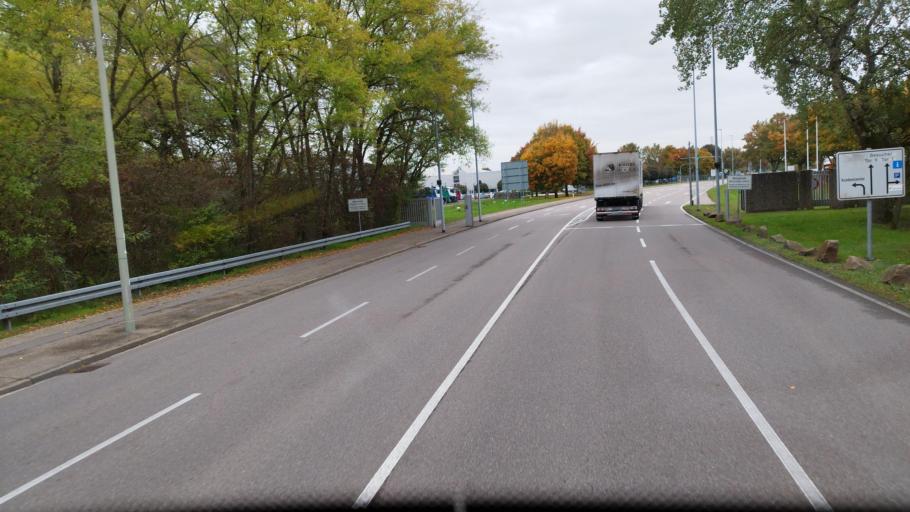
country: DE
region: Rheinland-Pfalz
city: Worth am Rhein
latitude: 49.0525
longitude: 8.2767
